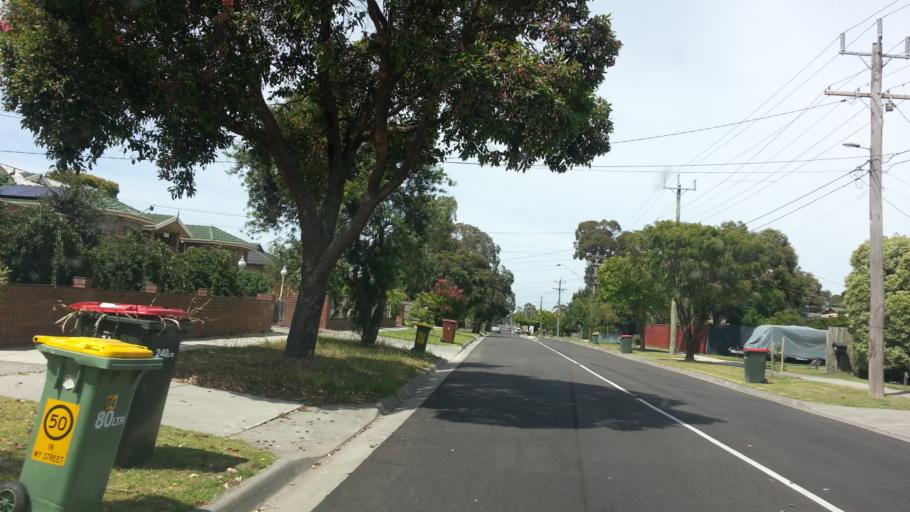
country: AU
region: Victoria
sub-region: Knox
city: Boronia
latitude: -37.8729
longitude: 145.2717
